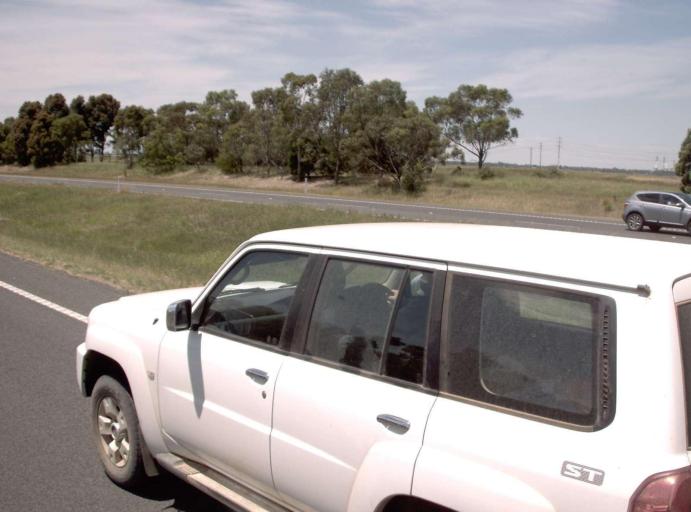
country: AU
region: Victoria
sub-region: Latrobe
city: Morwell
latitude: -38.2371
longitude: 146.4512
